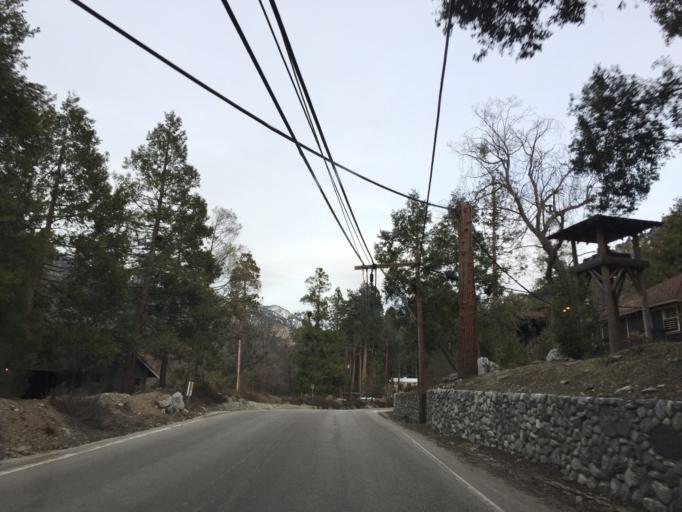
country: US
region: California
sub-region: San Bernardino County
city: Yucaipa
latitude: 34.0885
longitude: -116.9313
